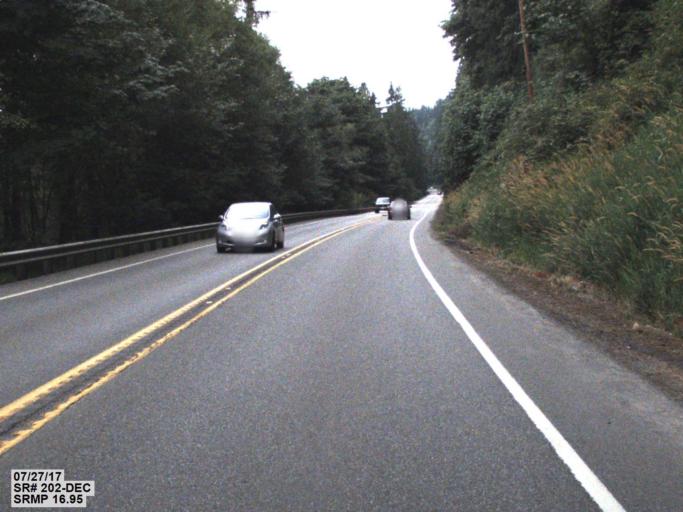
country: US
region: Washington
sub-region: King County
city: Ames Lake
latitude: 47.6052
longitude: -121.9609
